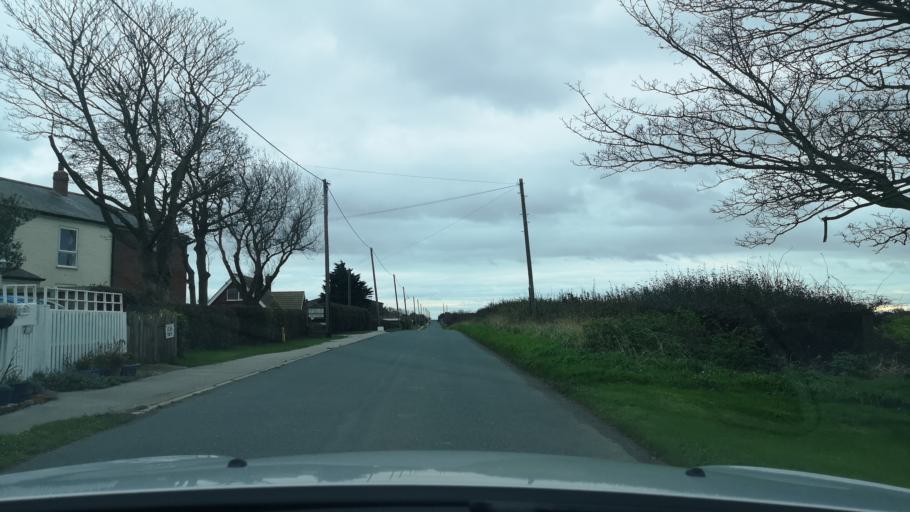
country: GB
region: England
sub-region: East Riding of Yorkshire
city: Easington
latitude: 53.6256
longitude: 0.1264
